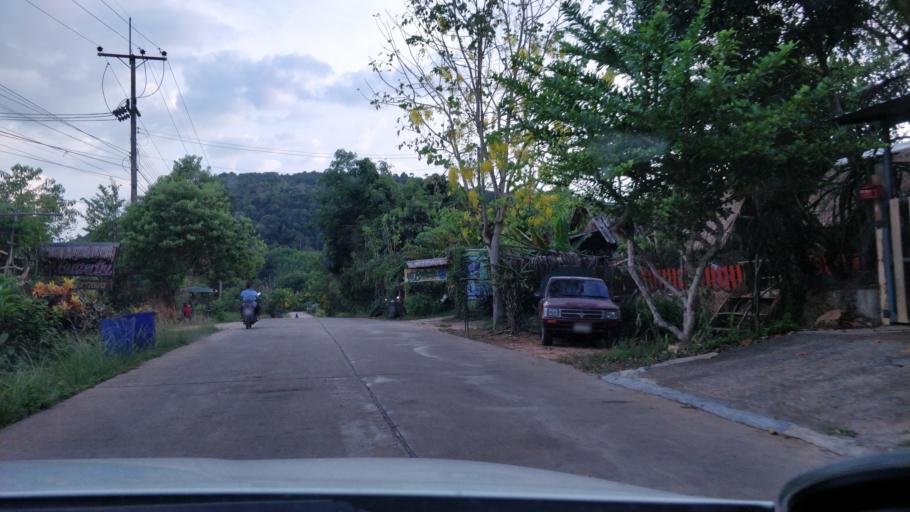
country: TH
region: Krabi
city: Saladan
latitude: 7.5846
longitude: 99.0683
